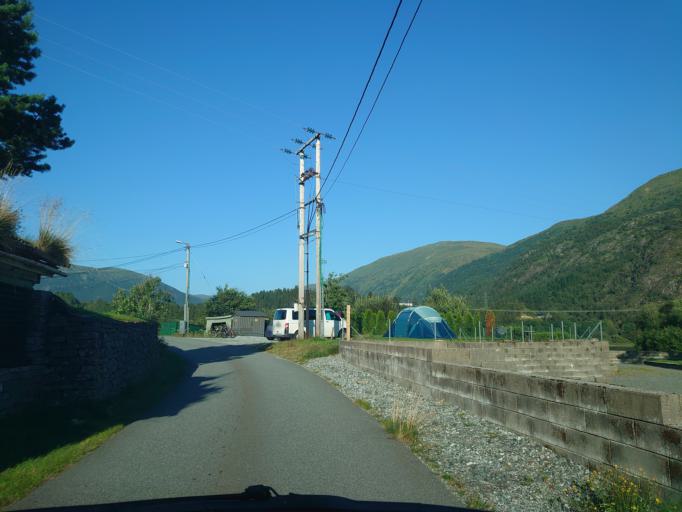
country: NO
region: Hordaland
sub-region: Bergen
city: Espeland
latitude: 60.3529
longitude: 5.4362
